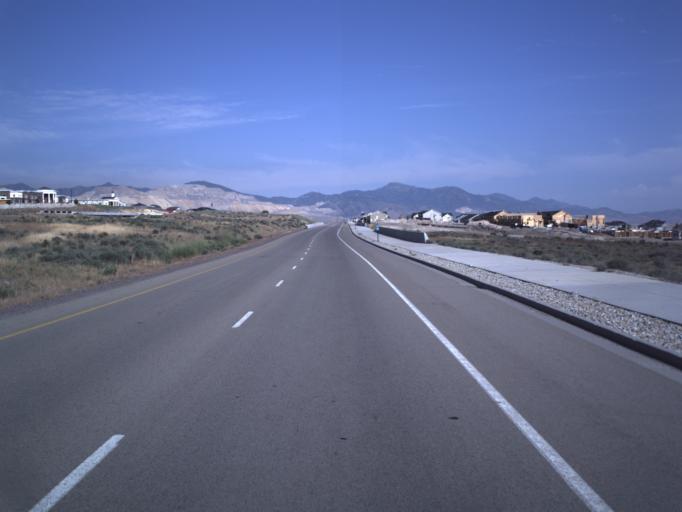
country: US
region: Utah
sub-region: Salt Lake County
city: Bluffdale
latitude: 40.4835
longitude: -111.9901
